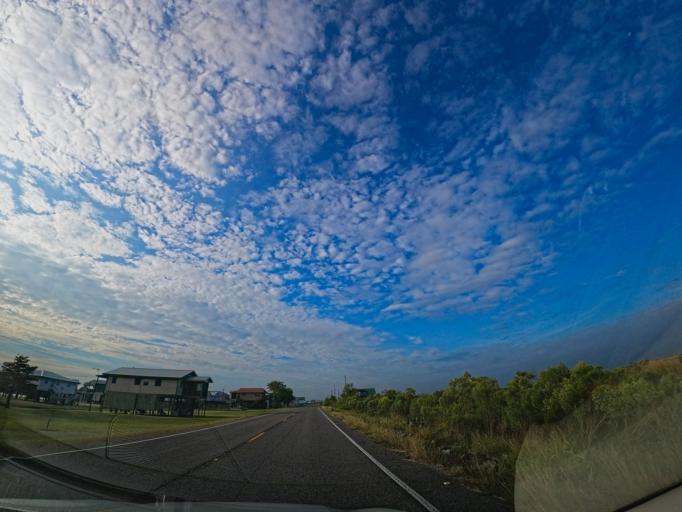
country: US
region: Louisiana
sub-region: Terrebonne Parish
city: Dulac
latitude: 29.3247
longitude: -90.6446
